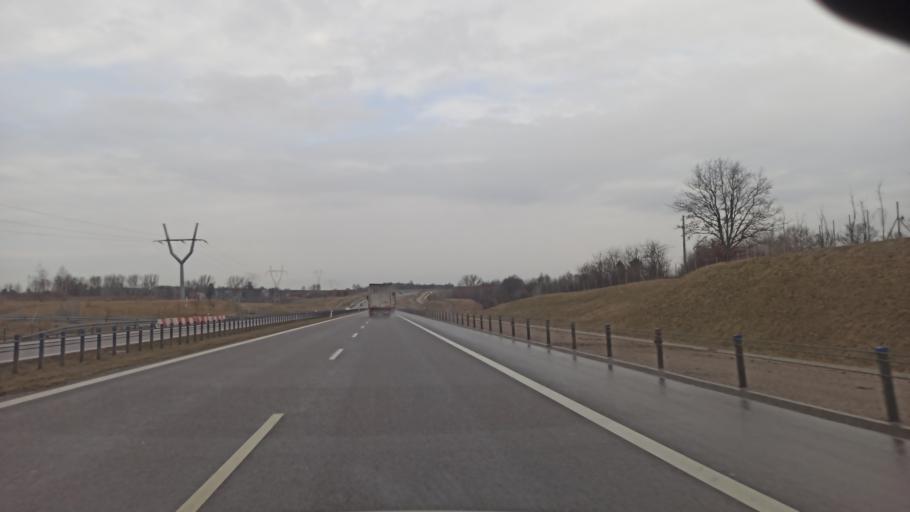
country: PL
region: Lublin Voivodeship
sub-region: Powiat lubelski
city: Kozubszczyzna
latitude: 51.2443
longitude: 22.4279
